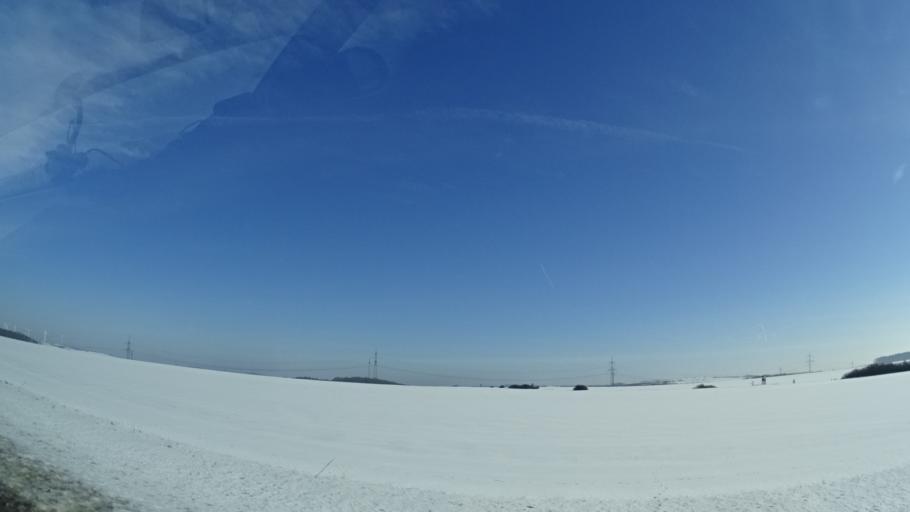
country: DE
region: Thuringia
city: Milda
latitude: 50.8691
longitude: 11.4590
